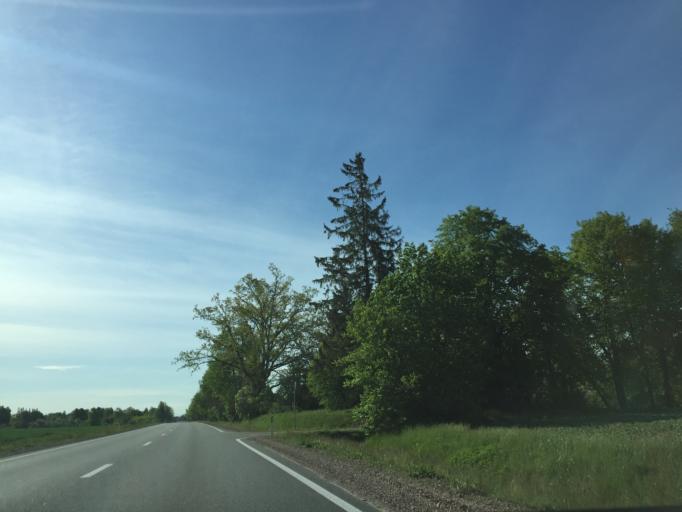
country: LV
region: Bauskas Rajons
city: Bauska
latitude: 56.3247
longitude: 24.3111
